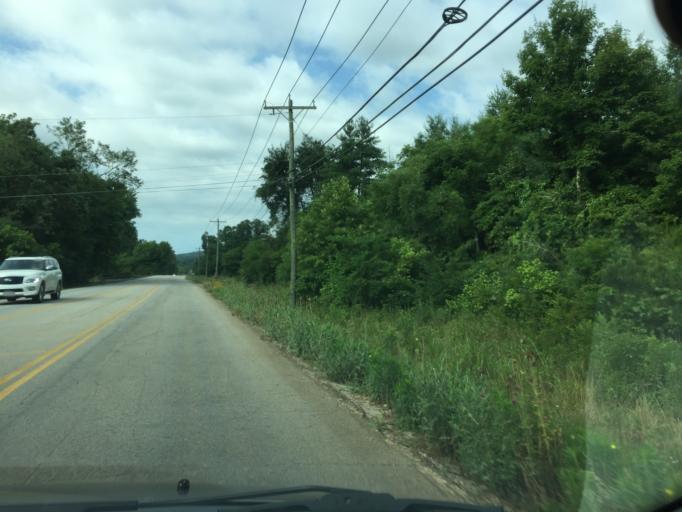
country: US
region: Tennessee
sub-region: Hamilton County
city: Apison
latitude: 34.9965
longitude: -85.0580
